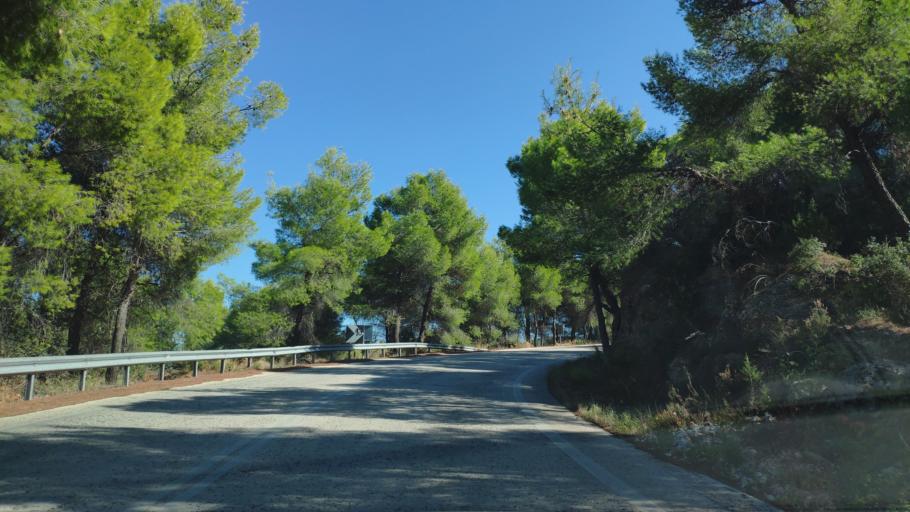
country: GR
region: Peloponnese
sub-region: Nomos Korinthias
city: Sofikon
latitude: 37.8289
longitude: 23.0508
